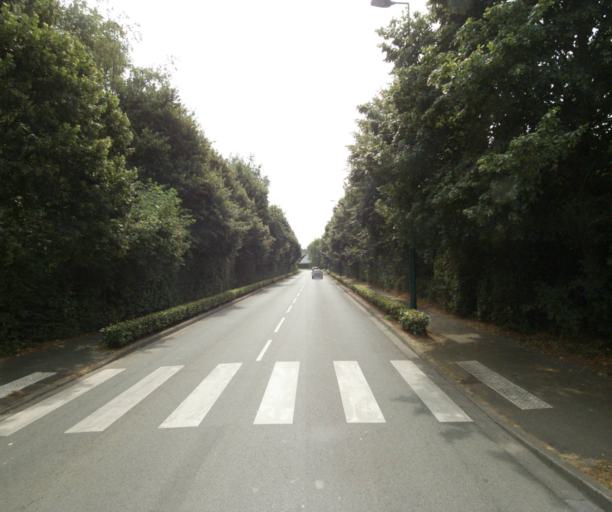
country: FR
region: Nord-Pas-de-Calais
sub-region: Departement du Nord
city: Mouvaux
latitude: 50.7139
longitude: 3.1282
